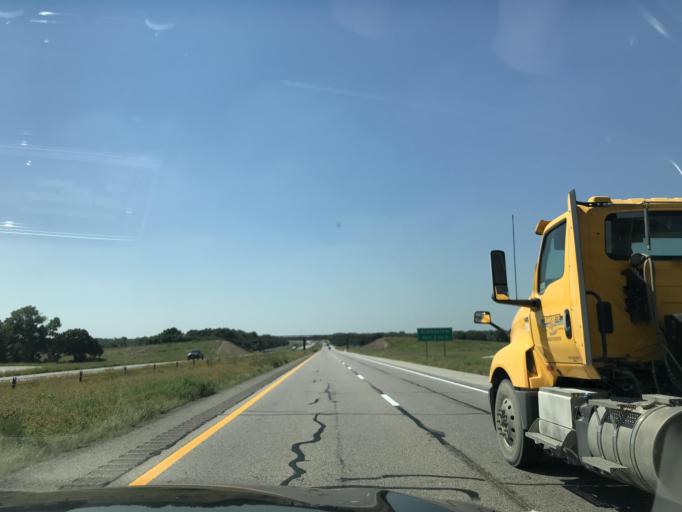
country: US
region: Texas
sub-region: Johnson County
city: Grandview
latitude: 32.3007
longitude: -97.1811
